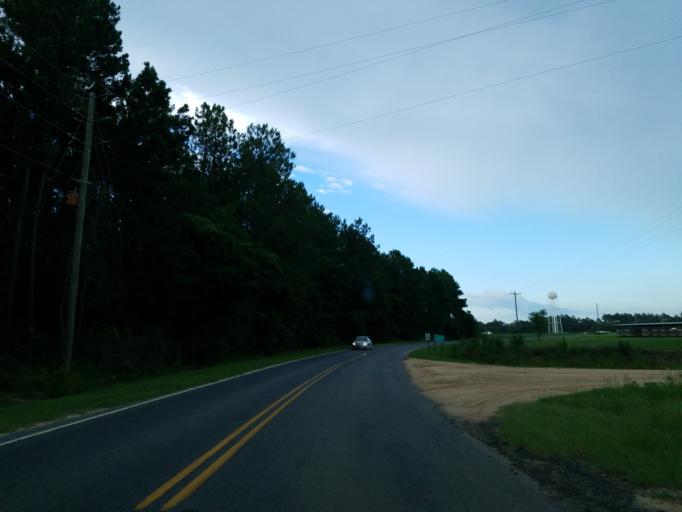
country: US
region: Georgia
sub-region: Cook County
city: Sparks
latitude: 31.2642
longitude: -83.4869
